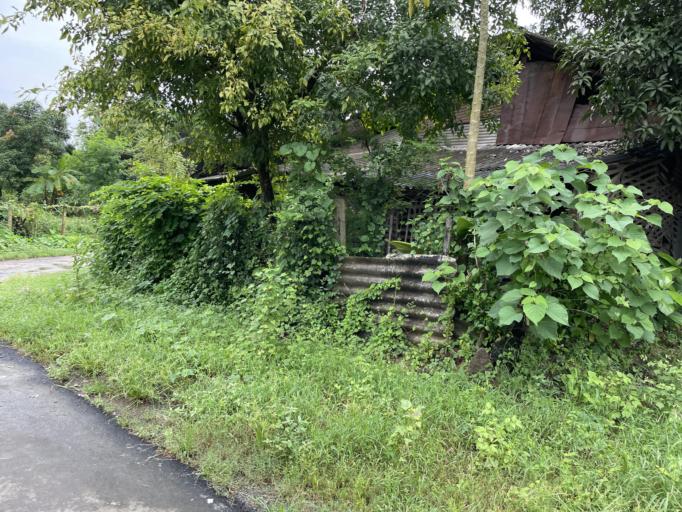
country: IN
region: Gujarat
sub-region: Valsad
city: Pardi
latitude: 20.4537
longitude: 72.9325
